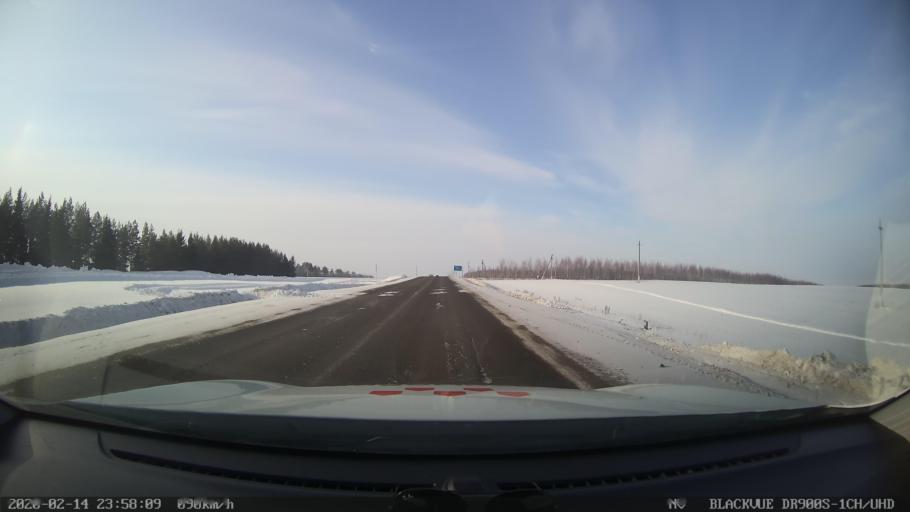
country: RU
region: Tatarstan
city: Kuybyshevskiy Zaton
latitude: 55.3390
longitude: 49.0937
